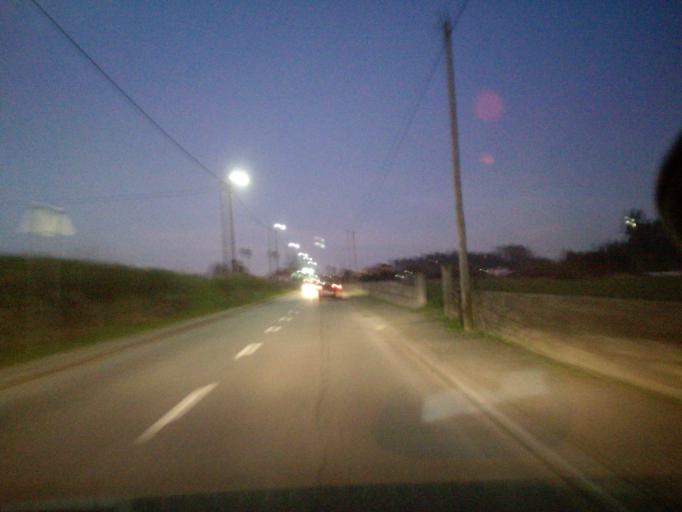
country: PT
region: Porto
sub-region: Maia
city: Nogueira
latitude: 41.2486
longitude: -8.5846
